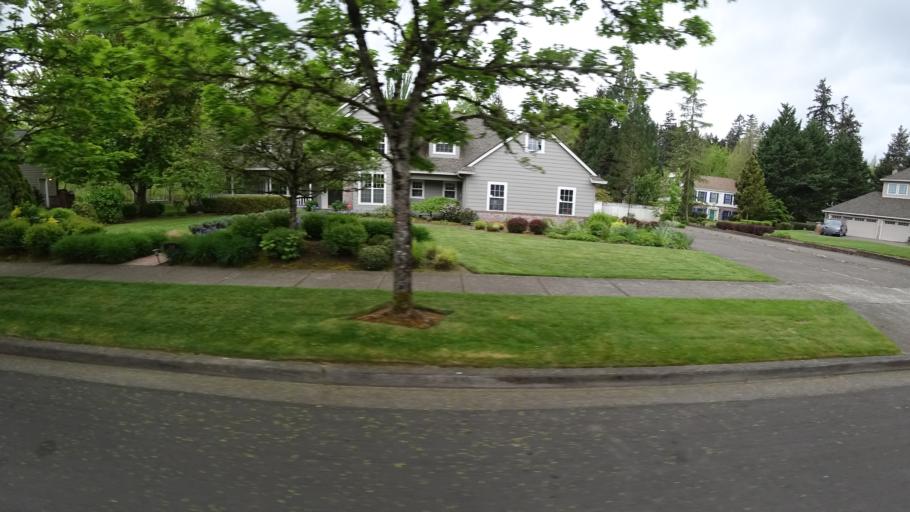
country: US
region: Oregon
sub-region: Washington County
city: Hillsboro
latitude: 45.5479
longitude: -122.9750
